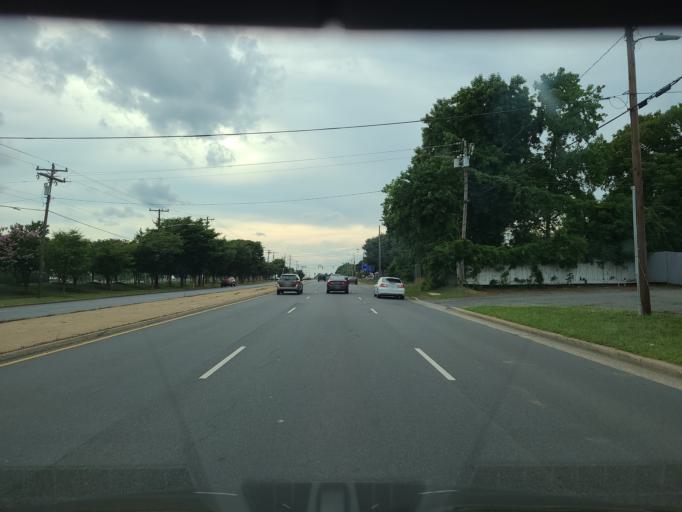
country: US
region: North Carolina
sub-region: Mecklenburg County
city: Charlotte
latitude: 35.2336
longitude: -80.9307
